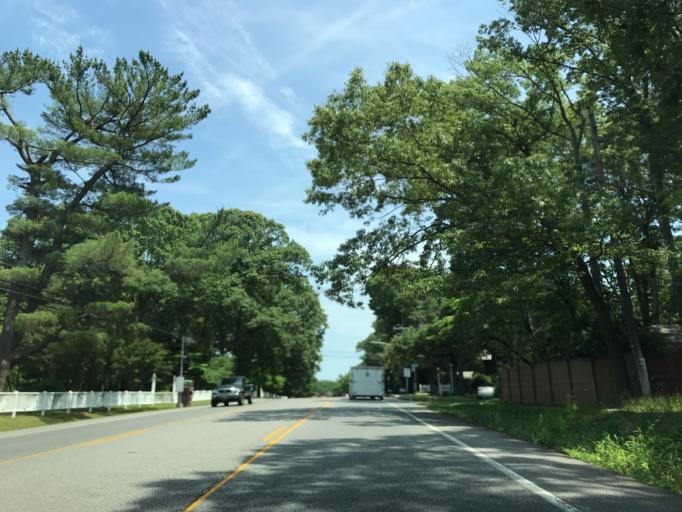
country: US
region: Maryland
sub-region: Anne Arundel County
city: Arden on the Severn
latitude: 39.0830
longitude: -76.5892
